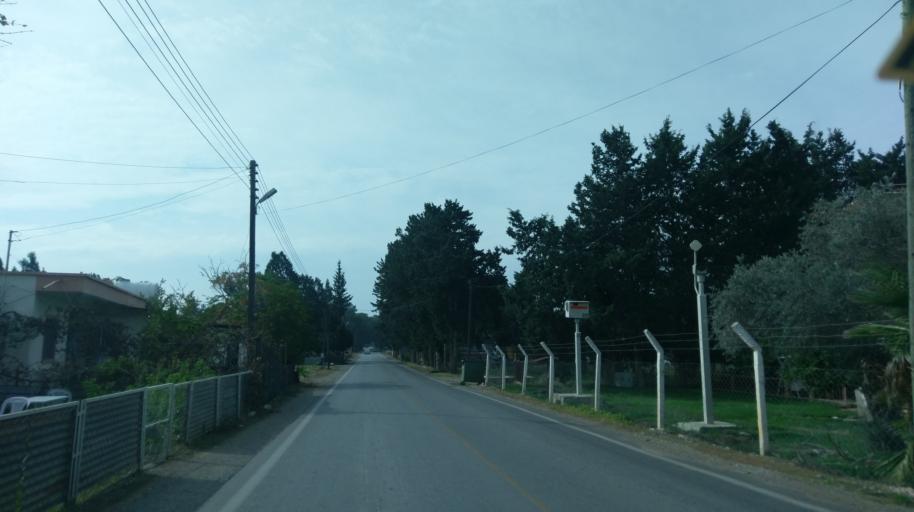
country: CY
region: Keryneia
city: Lapithos
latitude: 35.3141
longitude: 33.0685
